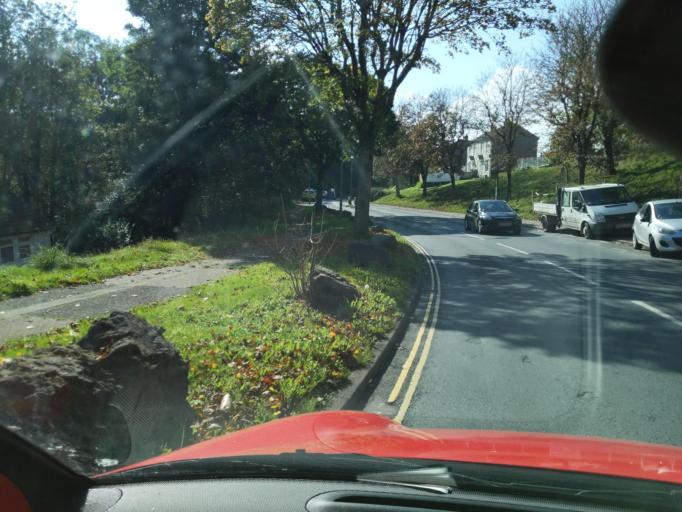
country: GB
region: England
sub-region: Plymouth
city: Plymouth
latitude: 50.4259
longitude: -4.1353
